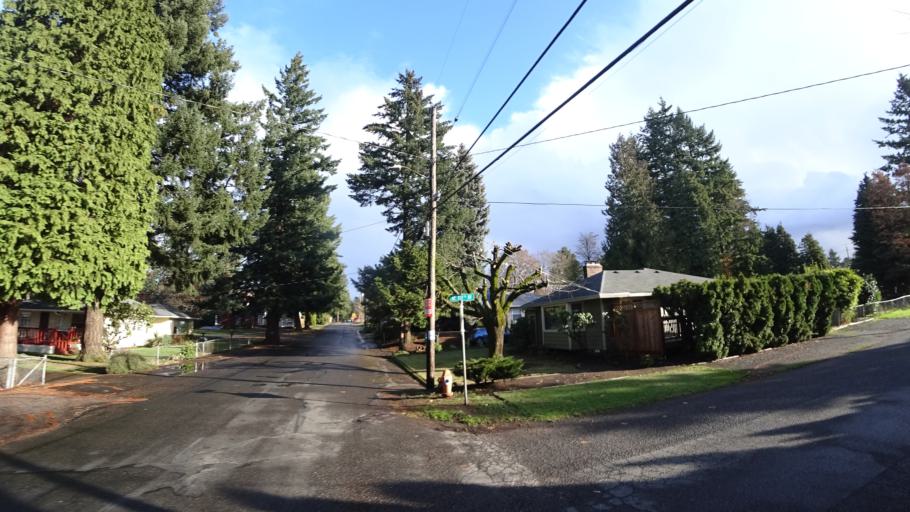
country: US
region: Oregon
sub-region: Multnomah County
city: Lents
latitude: 45.5281
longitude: -122.5467
